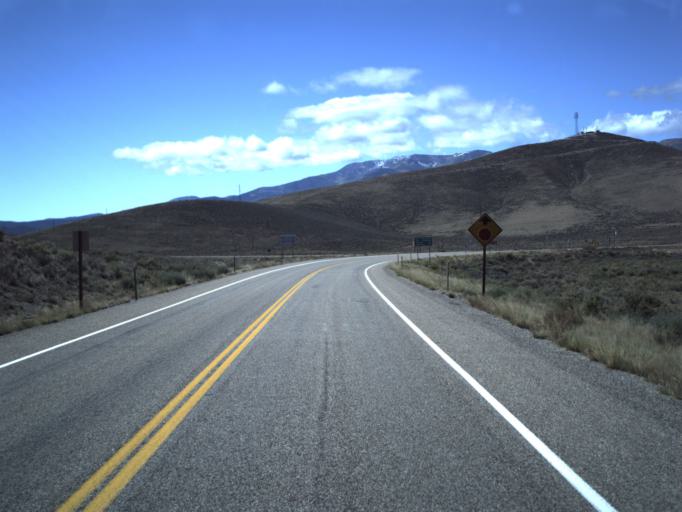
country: US
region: Utah
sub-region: Piute County
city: Junction
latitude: 38.2100
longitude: -112.2206
